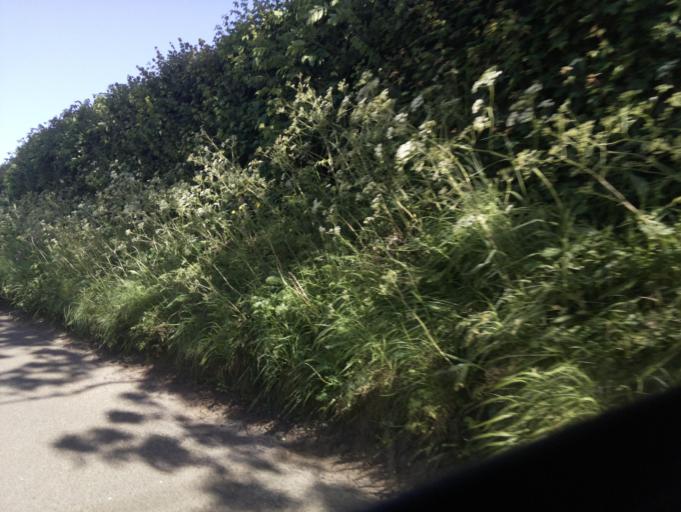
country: GB
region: England
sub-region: Somerset
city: Yeovil
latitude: 50.9336
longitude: -2.5822
